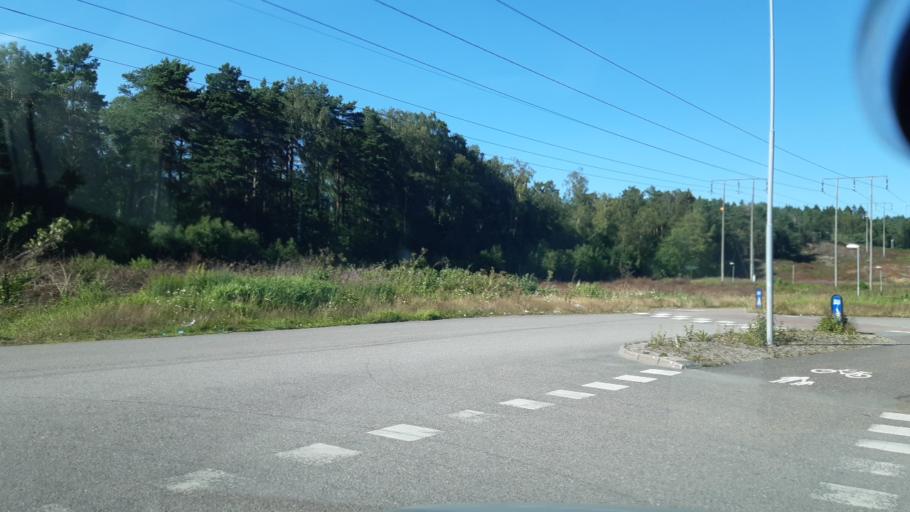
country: SE
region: Vaestra Goetaland
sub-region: Goteborg
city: Eriksbo
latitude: 57.7621
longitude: 12.0512
